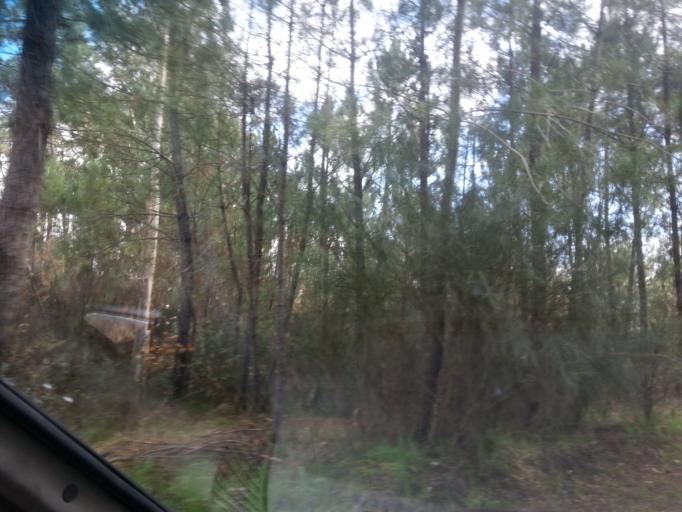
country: PT
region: Guarda
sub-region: Fornos de Algodres
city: Fornos de Algodres
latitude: 40.6264
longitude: -7.5236
